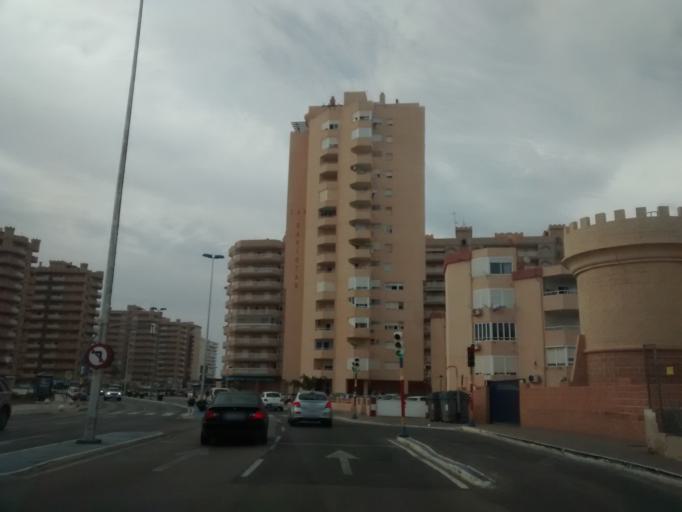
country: ES
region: Murcia
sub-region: Murcia
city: La Manga del Mar Menor
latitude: 37.6765
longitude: -0.7316
